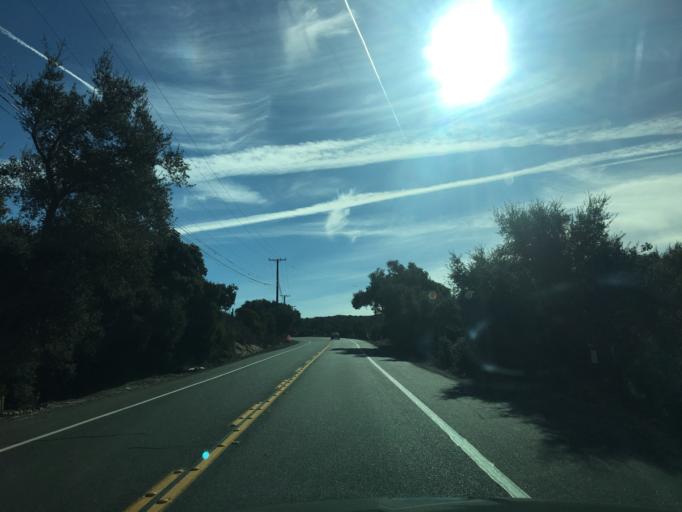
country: US
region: California
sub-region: Orange County
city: Foothill Ranch
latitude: 33.7546
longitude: -117.6947
